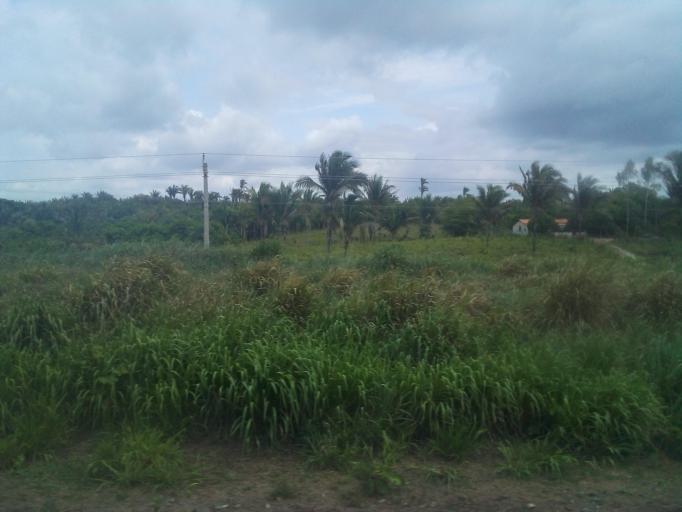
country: BR
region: Maranhao
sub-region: Santa Ines
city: Santa Ines
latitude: -3.7025
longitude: -45.9301
